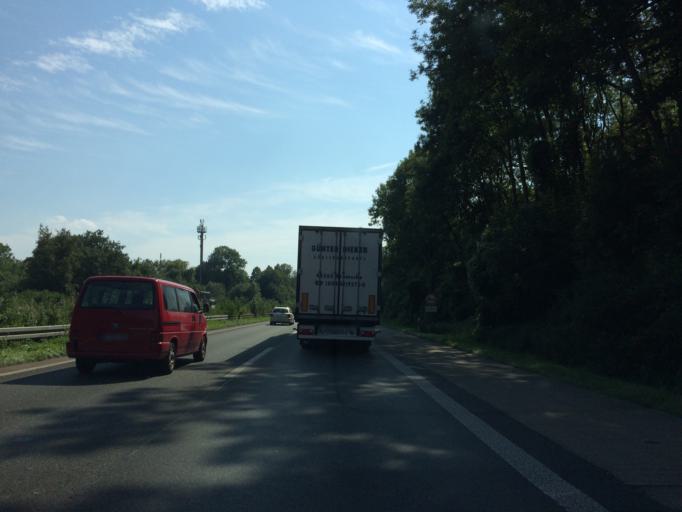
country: DE
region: North Rhine-Westphalia
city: Kamen
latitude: 51.6163
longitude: 7.6900
